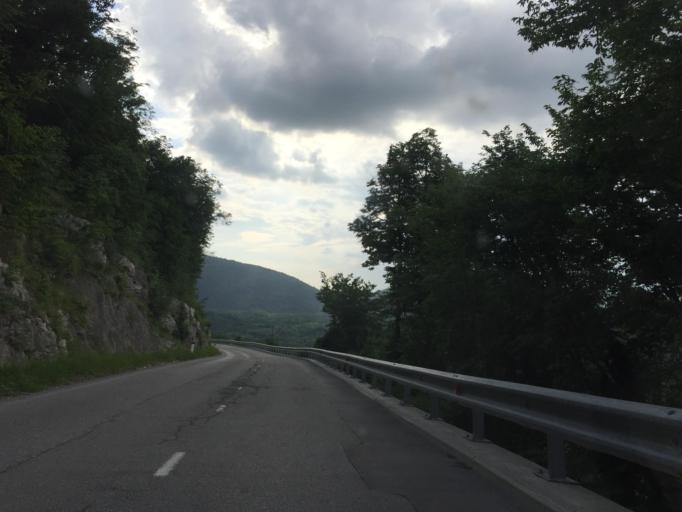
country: SI
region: Nova Gorica
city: Kromberk
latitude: 46.0080
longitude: 13.6947
